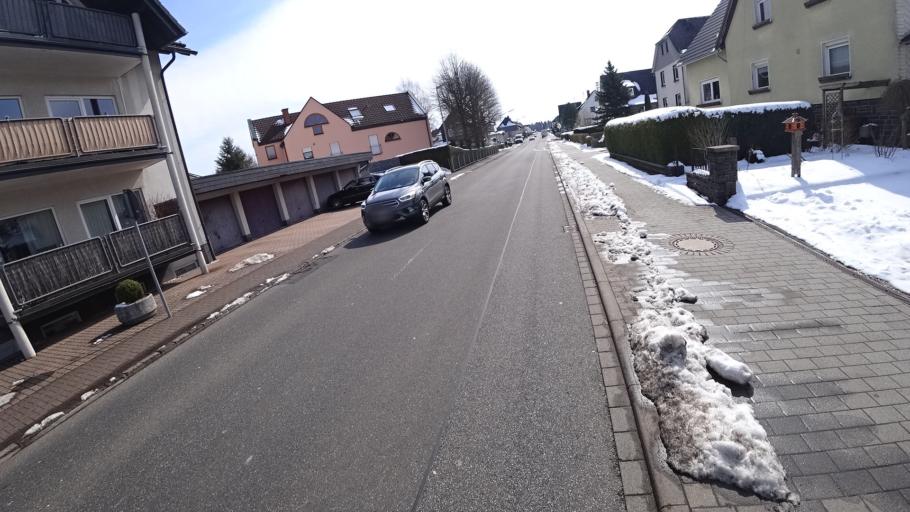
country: DE
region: Rheinland-Pfalz
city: Elkenroth
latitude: 50.7255
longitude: 7.8840
